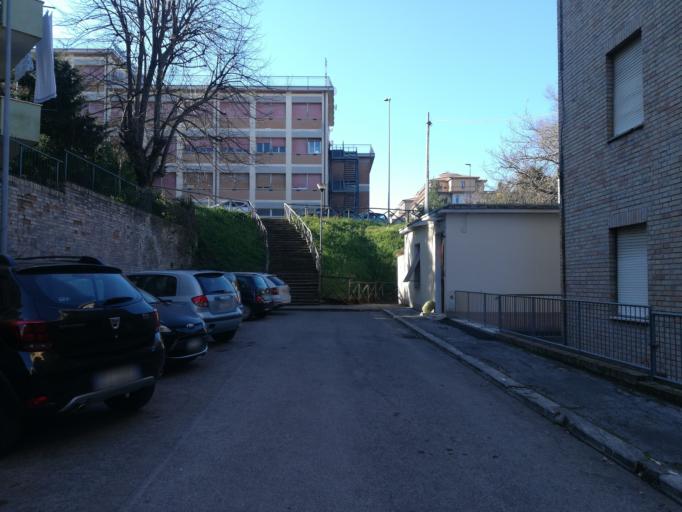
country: IT
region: The Marches
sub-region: Provincia di Macerata
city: Macerata
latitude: 43.3012
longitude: 13.4376
